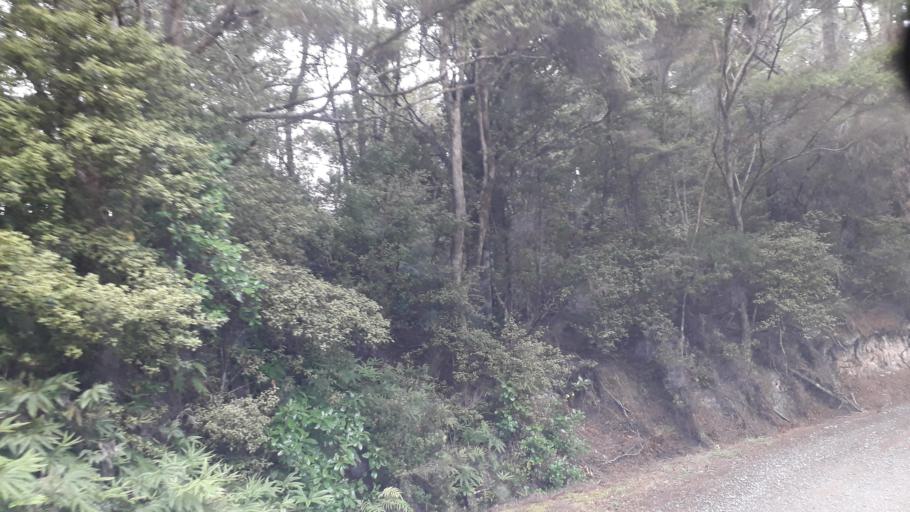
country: NZ
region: Northland
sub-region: Far North District
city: Waimate North
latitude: -35.3179
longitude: 173.5775
